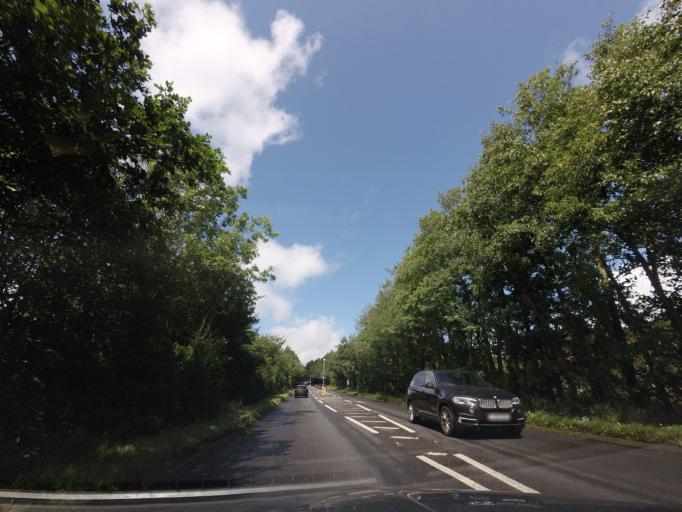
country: GB
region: England
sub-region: Kent
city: East Peckham
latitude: 51.2388
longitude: 0.3794
